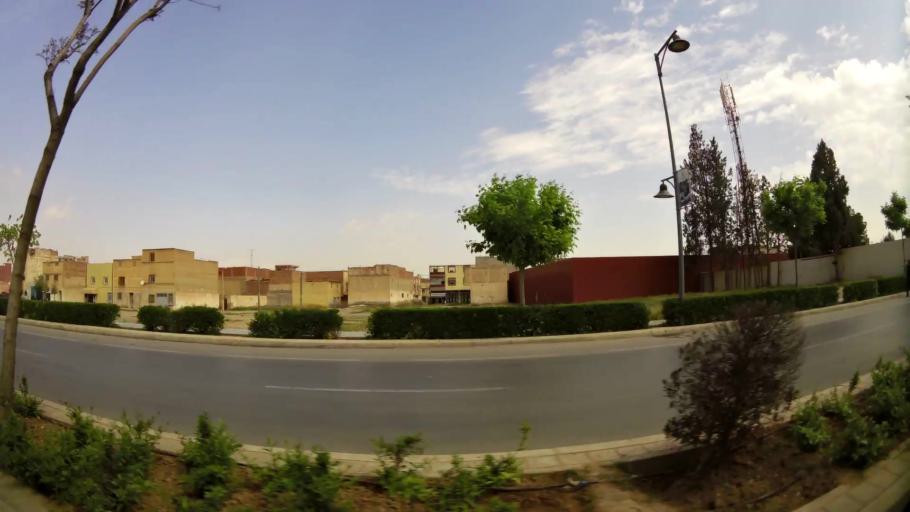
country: MA
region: Oriental
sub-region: Oujda-Angad
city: Oujda
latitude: 34.6791
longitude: -1.8973
